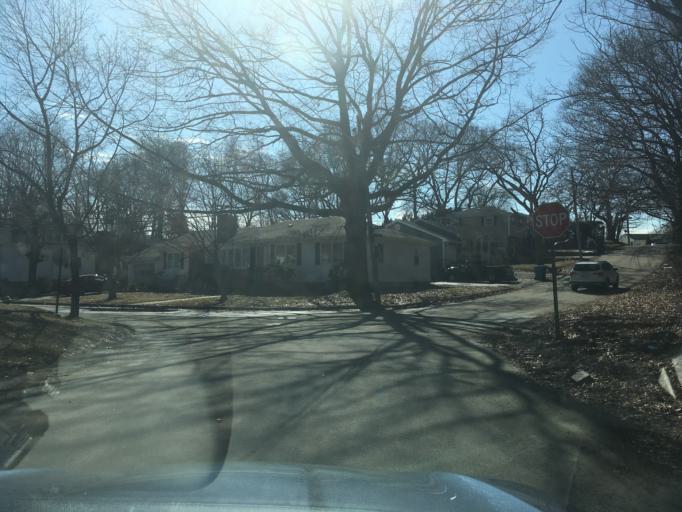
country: US
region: Rhode Island
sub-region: Providence County
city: Cranston
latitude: 41.7859
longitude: -71.4411
